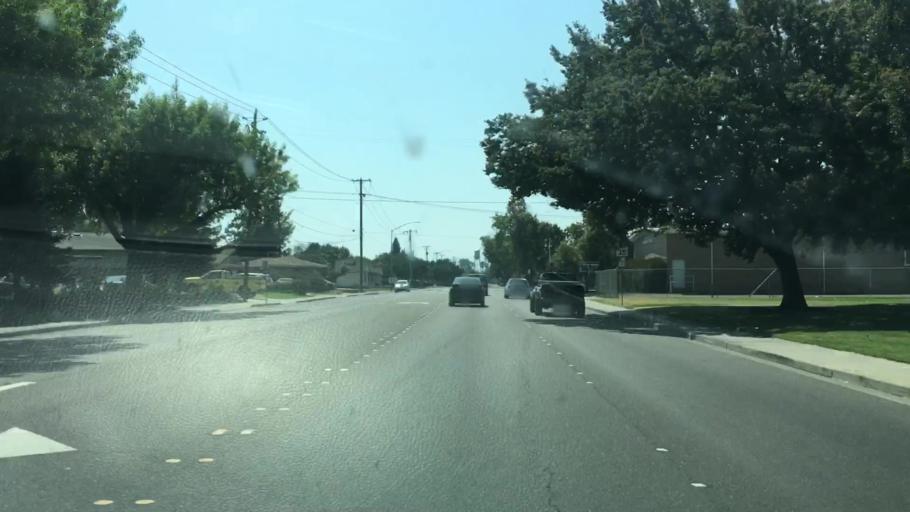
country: US
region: California
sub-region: San Joaquin County
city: Tracy
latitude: 37.7474
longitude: -121.4351
